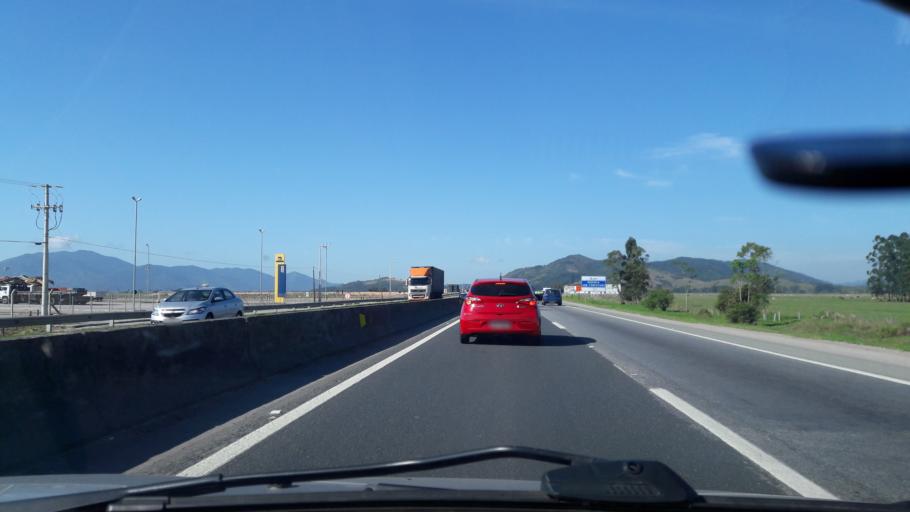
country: BR
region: Santa Catarina
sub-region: Tijucas
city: Tijucas
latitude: -27.2486
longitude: -48.6311
